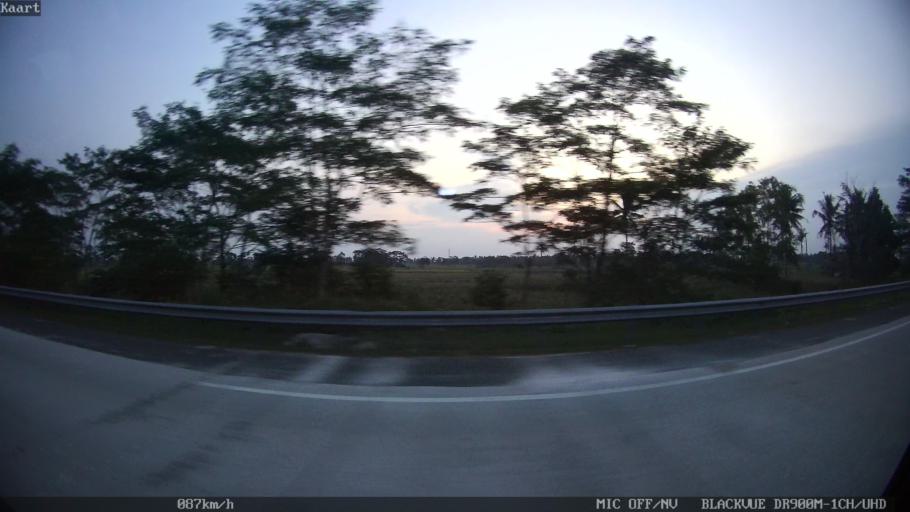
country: ID
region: Lampung
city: Sidorejo
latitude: -5.6298
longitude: 105.5666
